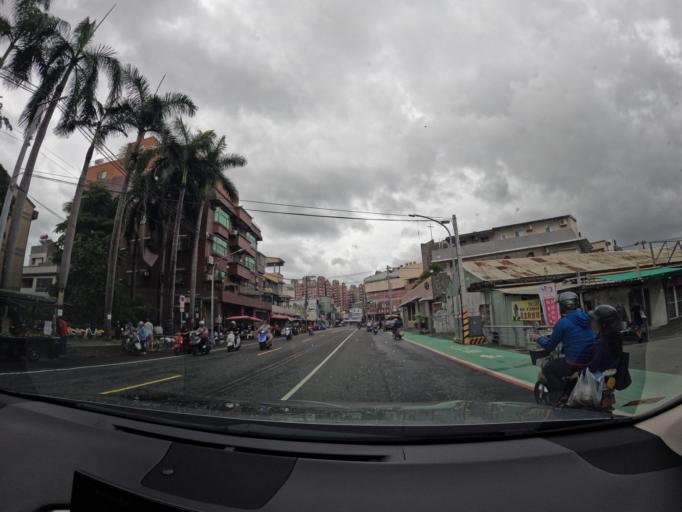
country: TW
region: Taiwan
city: Fengshan
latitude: 22.6275
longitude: 120.3738
